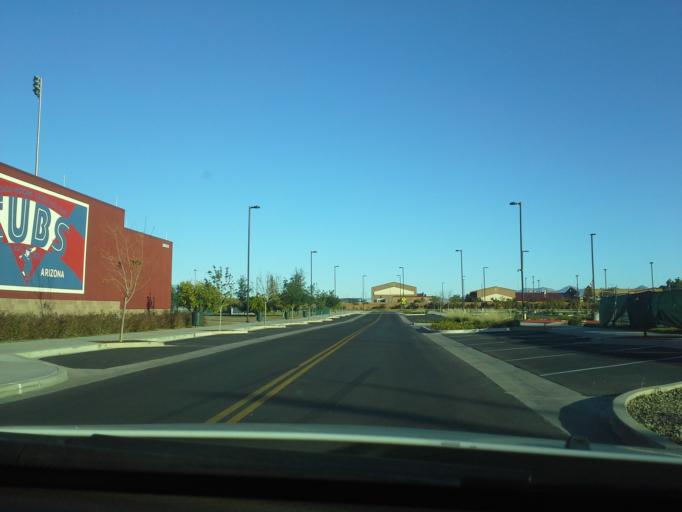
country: US
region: Arizona
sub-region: Maricopa County
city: Tempe
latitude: 33.4309
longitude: -111.8802
